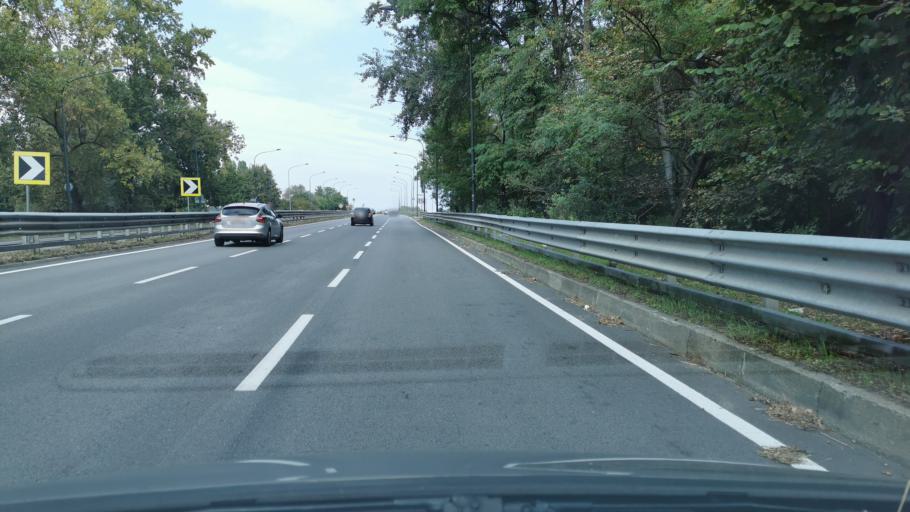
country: IT
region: Piedmont
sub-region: Provincia di Torino
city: San Mauro Torinese
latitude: 45.0900
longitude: 7.7276
